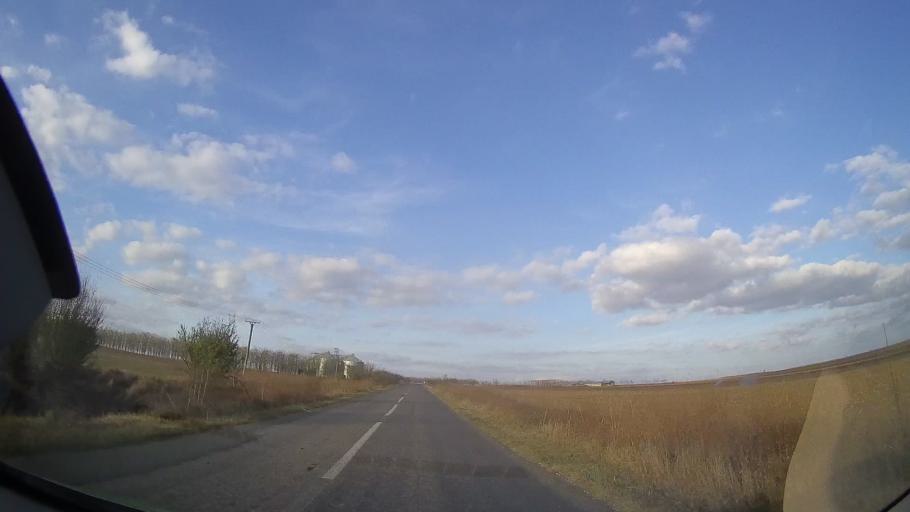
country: RO
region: Constanta
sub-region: Comuna Dumbraveni
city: Dumbraveni
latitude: 43.9235
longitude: 28.0296
